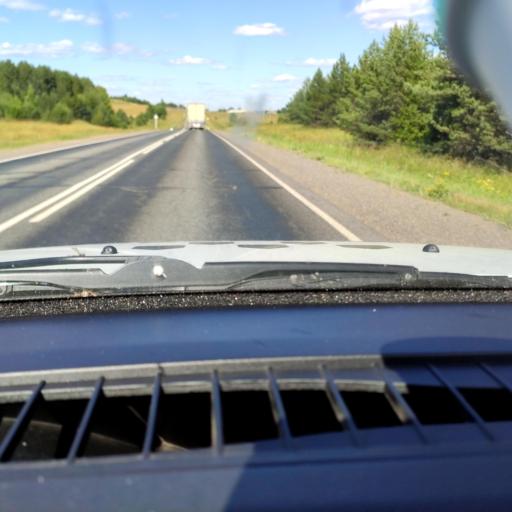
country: RU
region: Udmurtiya
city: Votkinsk
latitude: 57.3702
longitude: 54.4276
